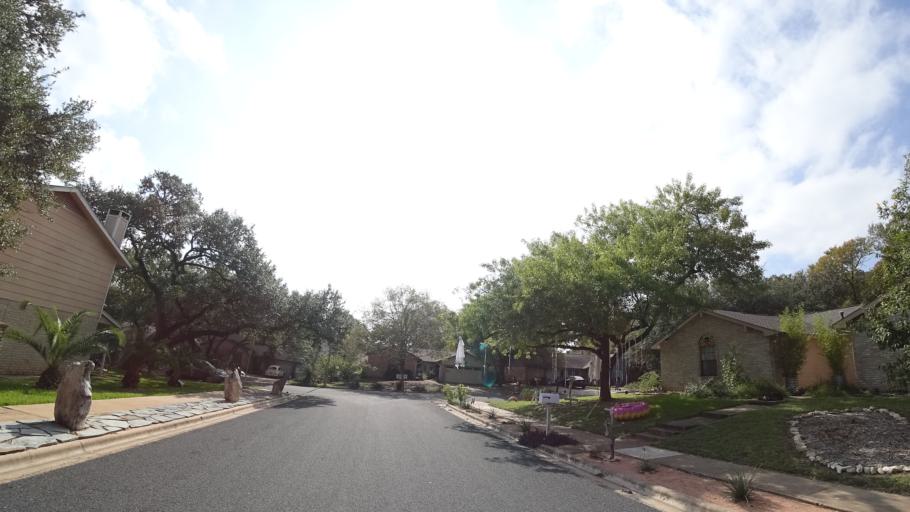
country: US
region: Texas
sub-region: Travis County
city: Shady Hollow
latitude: 30.2028
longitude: -97.8211
